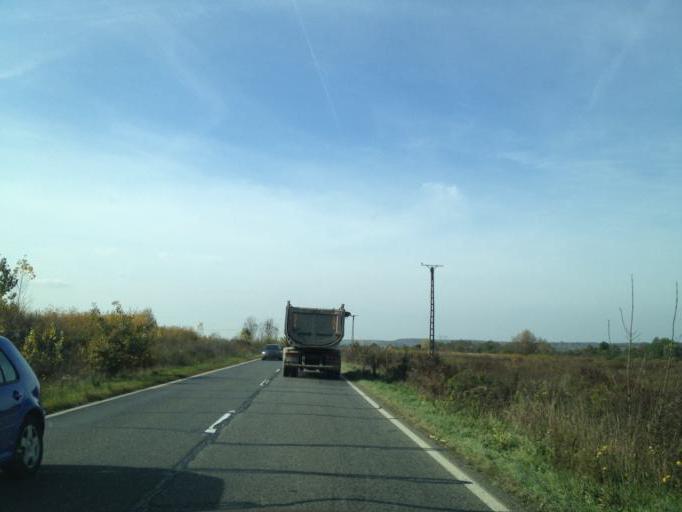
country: RO
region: Timis
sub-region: Comuna Faget
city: Faget
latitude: 45.8579
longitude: 22.2227
